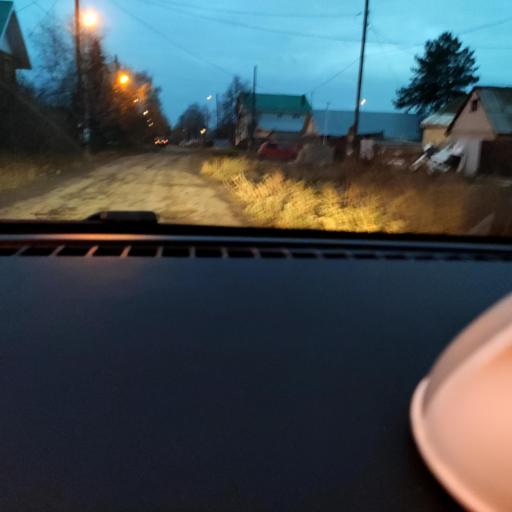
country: RU
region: Samara
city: Smyshlyayevka
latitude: 53.2527
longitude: 50.3533
